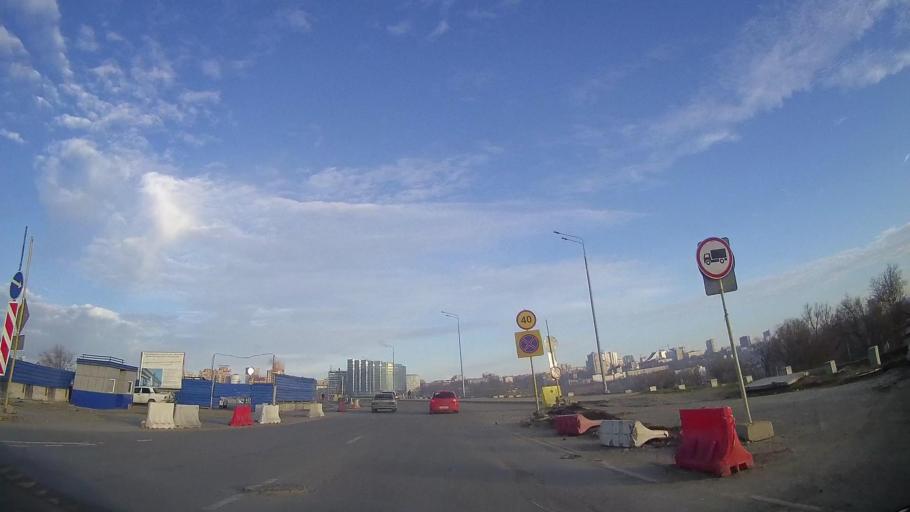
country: RU
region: Rostov
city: Rostov-na-Donu
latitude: 47.2105
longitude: 39.7247
